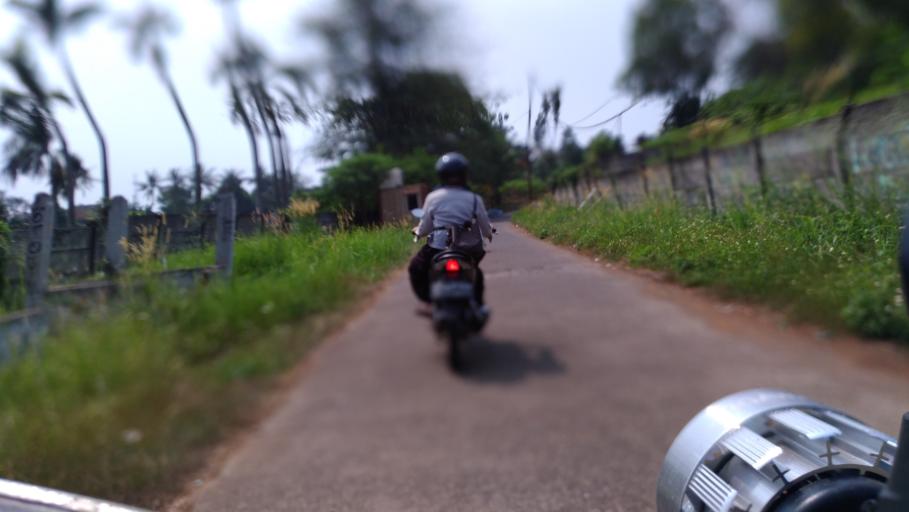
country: ID
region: West Java
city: Cileungsir
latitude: -6.3560
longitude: 106.8957
